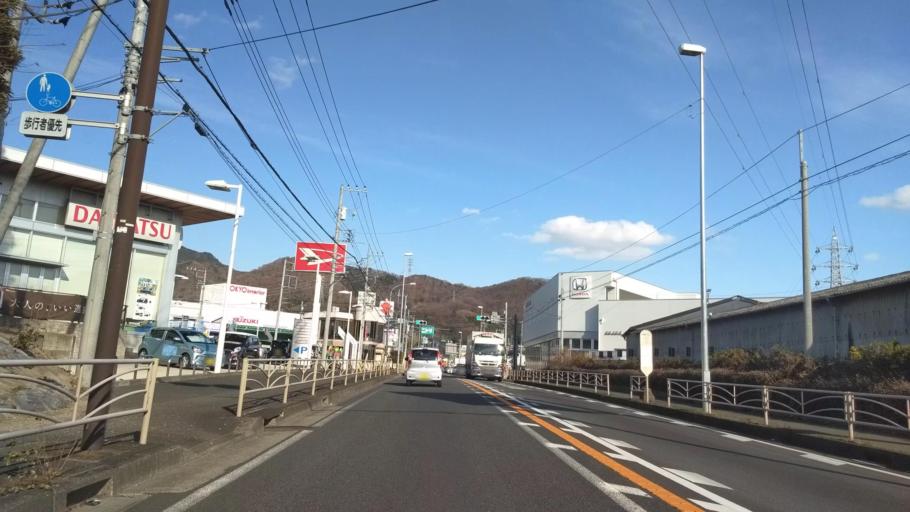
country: JP
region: Kanagawa
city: Hadano
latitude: 35.3806
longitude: 139.2377
